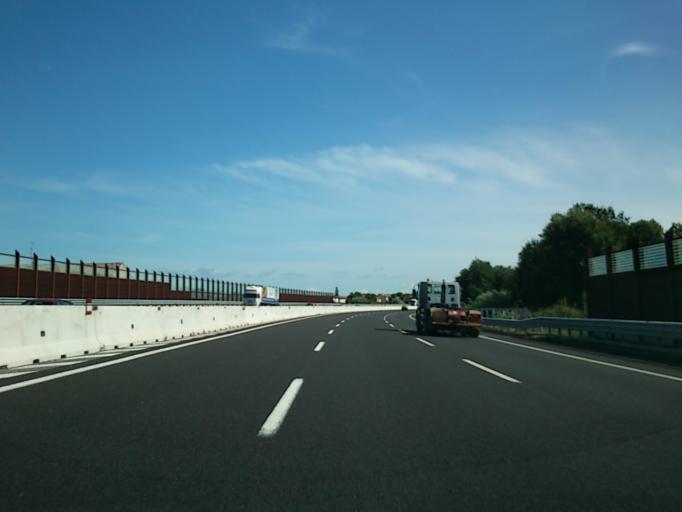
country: IT
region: The Marches
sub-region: Provincia di Pesaro e Urbino
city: Centinarola
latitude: 43.8373
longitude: 12.9891
